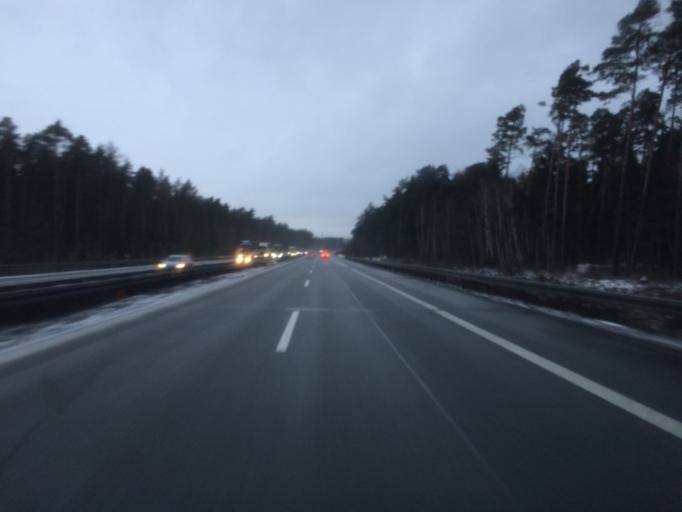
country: DE
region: Bavaria
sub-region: Upper Palatinate
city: Teublitz
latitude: 49.2503
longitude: 12.1280
